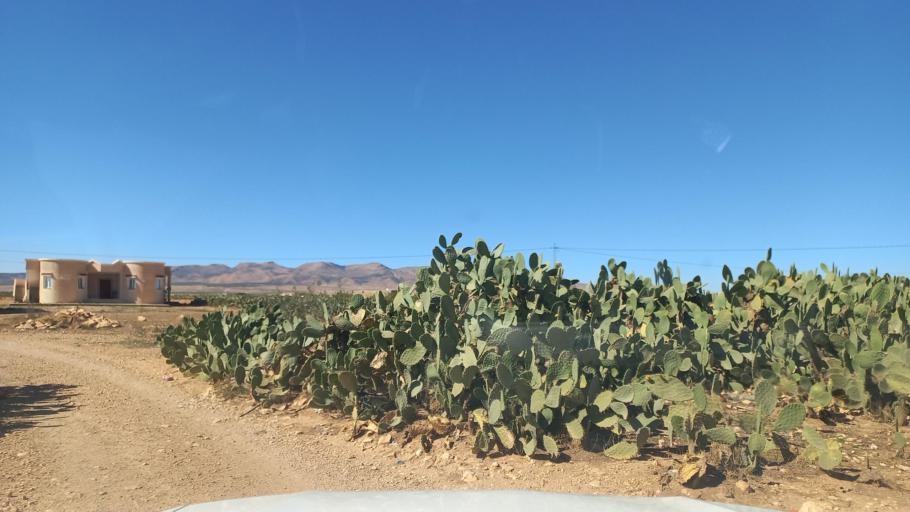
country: TN
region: Al Qasrayn
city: Sbiba
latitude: 35.3825
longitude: 9.0911
